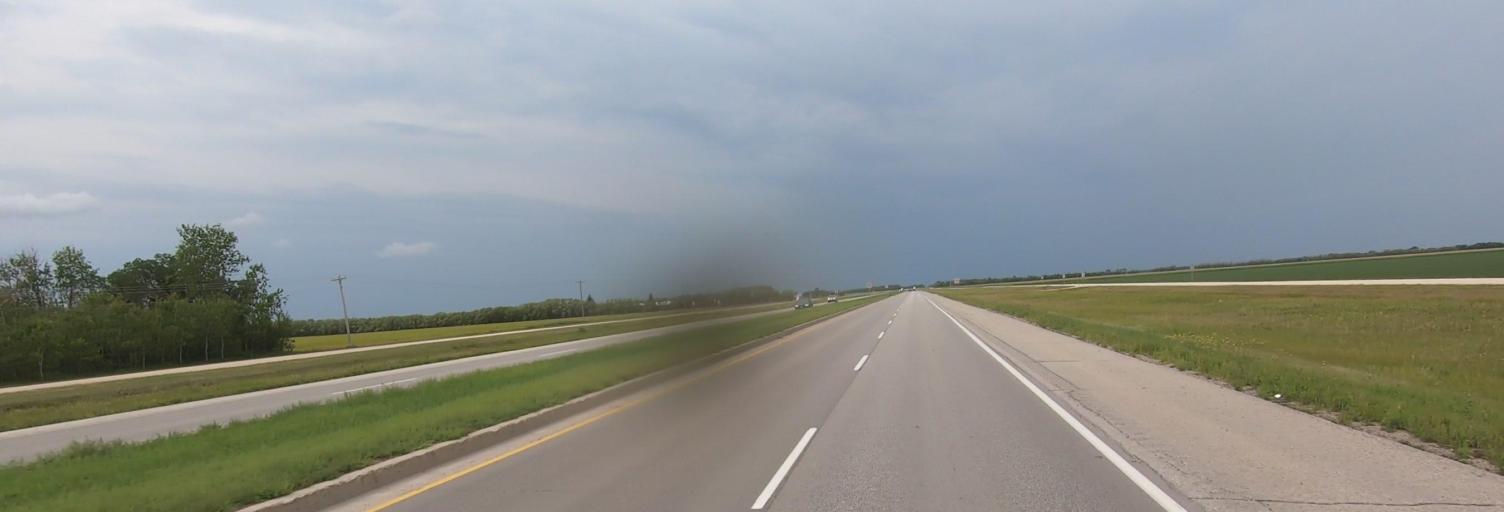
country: CA
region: Manitoba
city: Winnipeg
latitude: 49.7680
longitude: -97.2577
